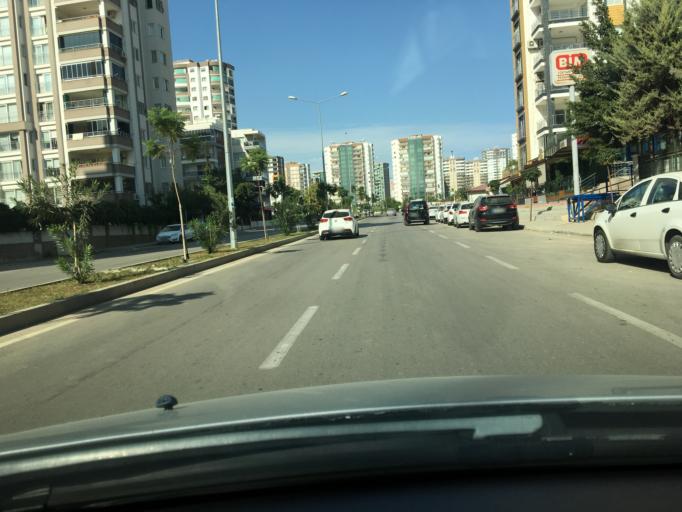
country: TR
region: Adana
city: Seyhan
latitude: 37.0204
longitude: 35.2583
